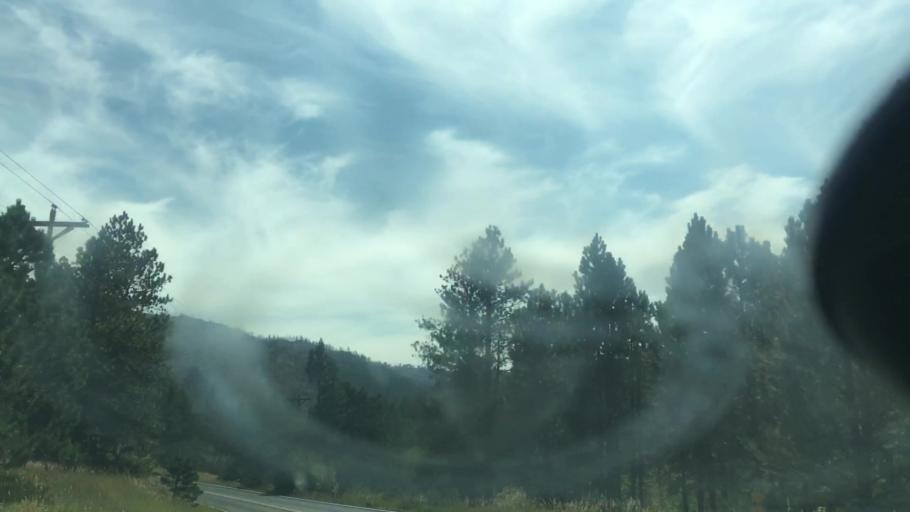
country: US
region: Colorado
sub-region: Larimer County
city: Laporte
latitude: 40.6058
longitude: -105.3471
